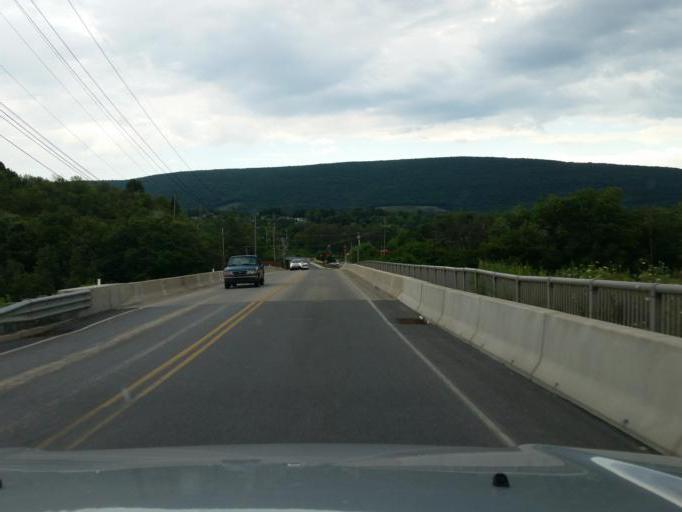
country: US
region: Pennsylvania
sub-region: Blair County
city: Greenwood
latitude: 40.5378
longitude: -78.3768
